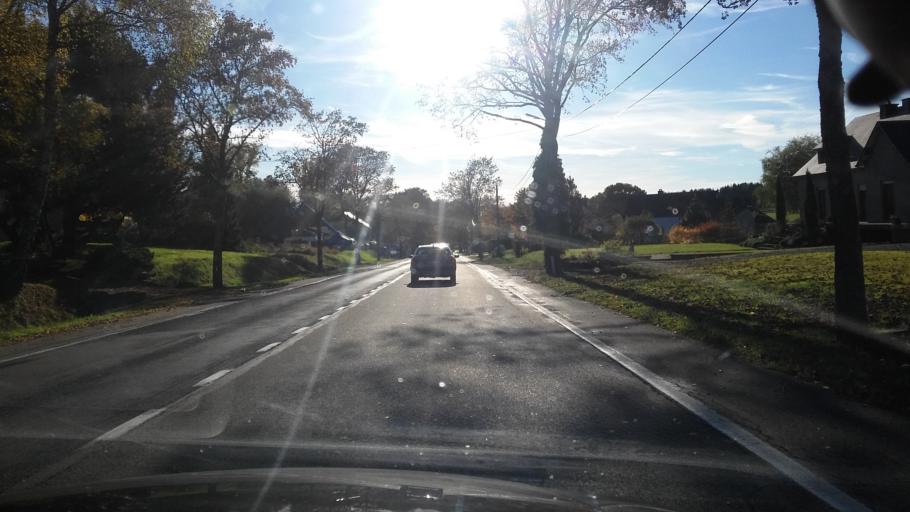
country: BE
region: Wallonia
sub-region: Province du Luxembourg
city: Chiny
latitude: 49.6880
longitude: 5.3841
